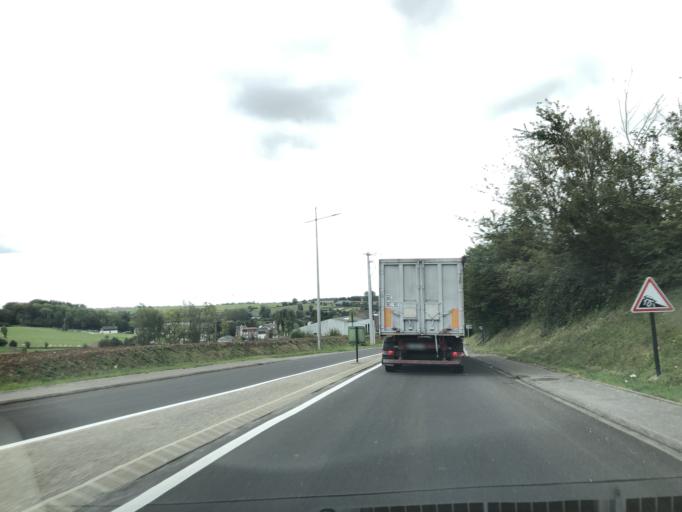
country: FR
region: Nord-Pas-de-Calais
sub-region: Departement du Pas-de-Calais
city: Fruges
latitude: 50.5212
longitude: 2.1328
